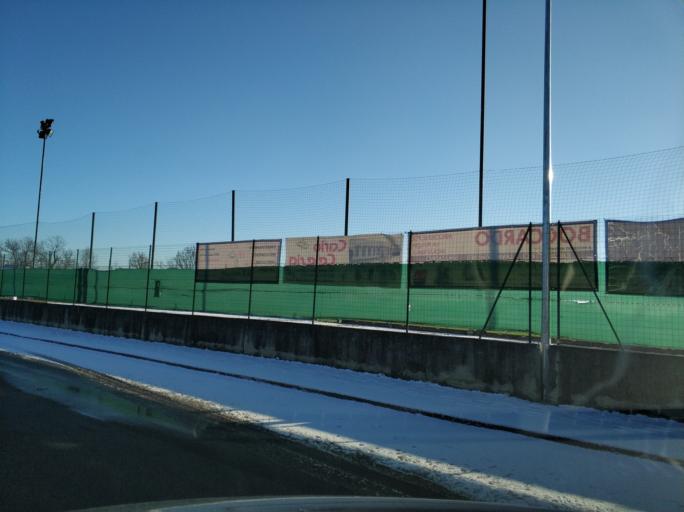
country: IT
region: Piedmont
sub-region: Provincia di Torino
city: San Francesco al Campo
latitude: 45.2377
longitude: 7.6543
